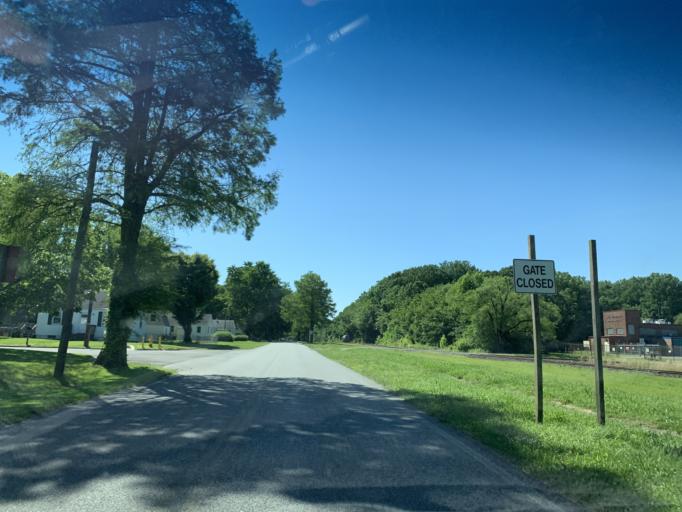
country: US
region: Maryland
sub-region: Harford County
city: Aberdeen
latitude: 39.5019
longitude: -76.1647
